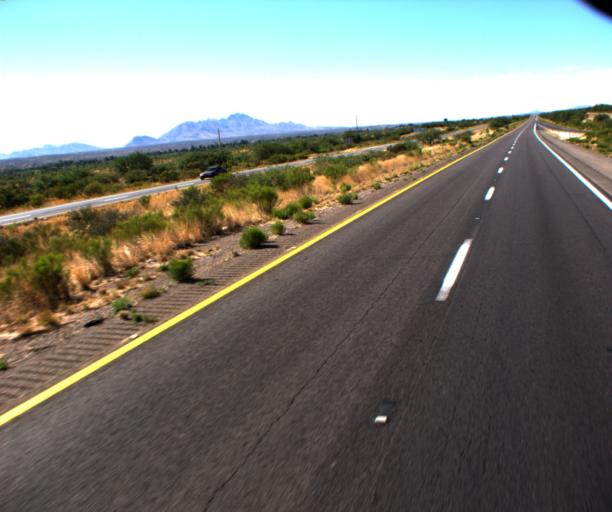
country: US
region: Arizona
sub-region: Santa Cruz County
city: Tubac
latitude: 31.6510
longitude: -111.0594
